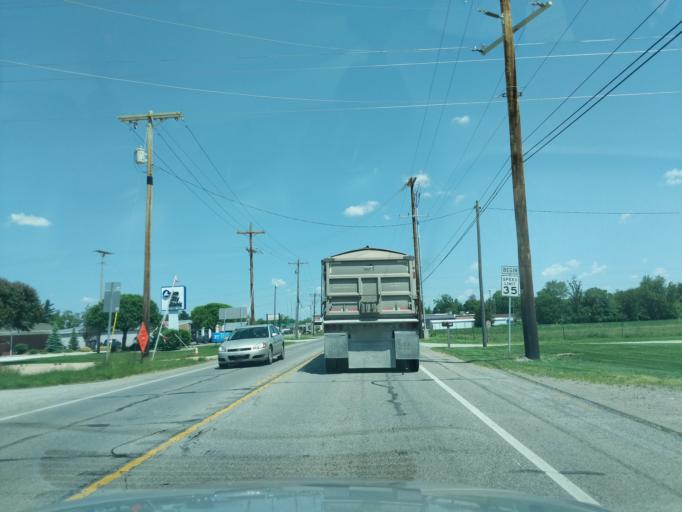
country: US
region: Indiana
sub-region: Noble County
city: Ligonier
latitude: 41.4494
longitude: -85.5862
